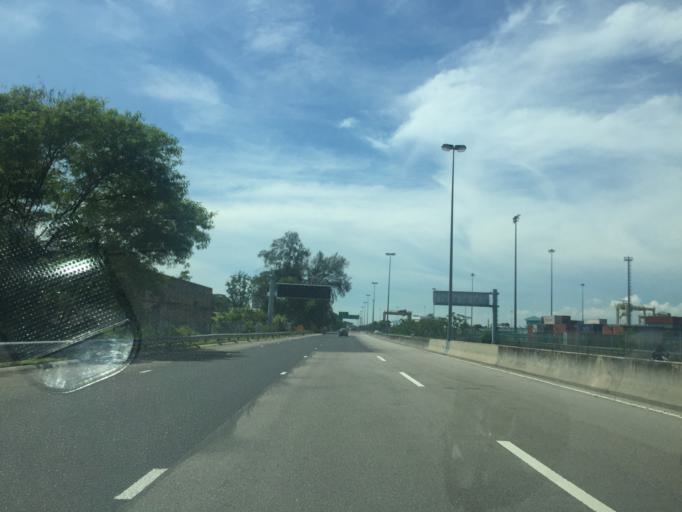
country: MY
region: Penang
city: Butterworth
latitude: 5.4171
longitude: 100.3721
